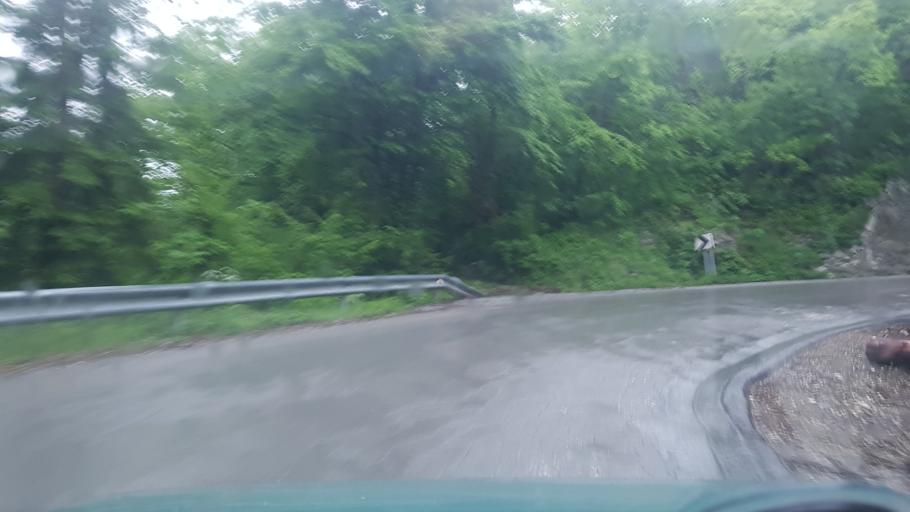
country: SI
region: Bohinj
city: Bohinjska Bistrica
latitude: 46.2755
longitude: 13.9634
